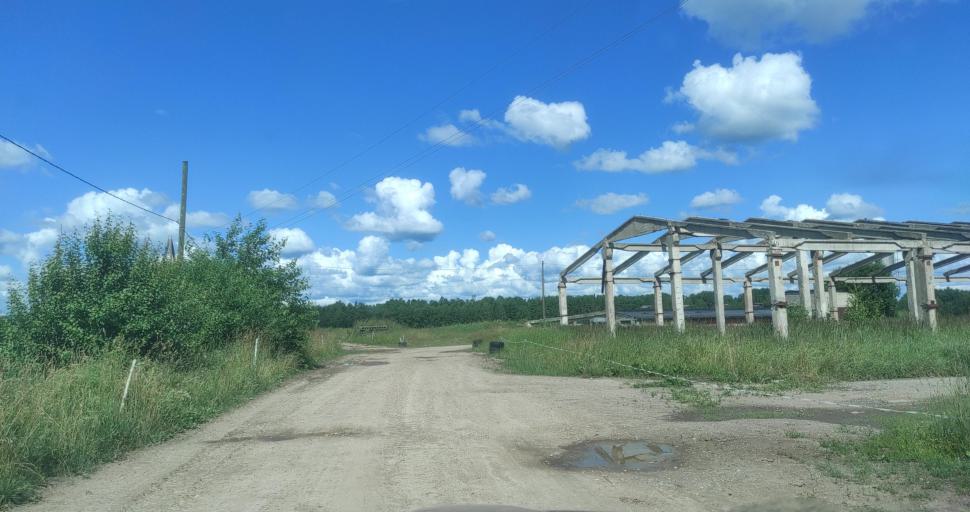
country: LV
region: Kuldigas Rajons
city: Kuldiga
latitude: 57.0019
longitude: 22.1294
